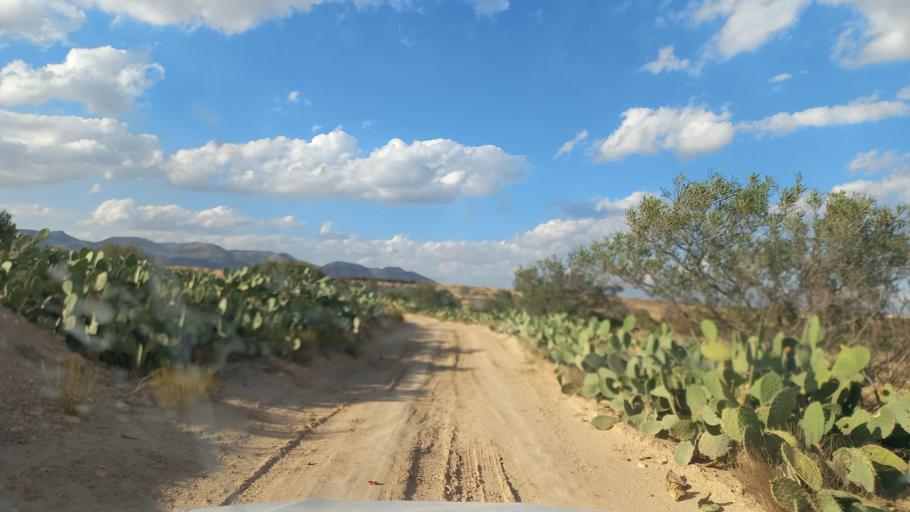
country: TN
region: Al Qasrayn
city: Sbiba
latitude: 35.3835
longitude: 9.0724
